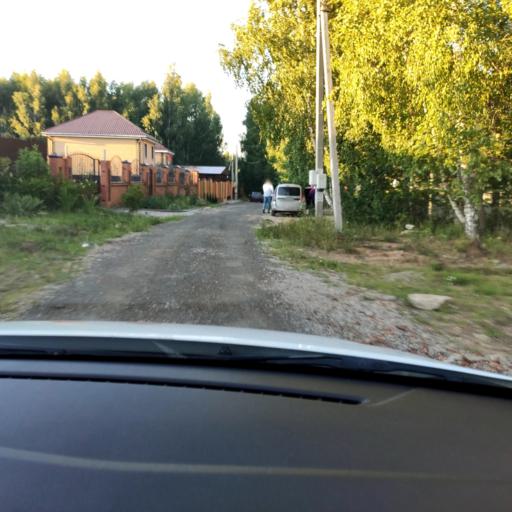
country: RU
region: Tatarstan
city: Stolbishchi
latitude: 55.7393
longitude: 49.2556
